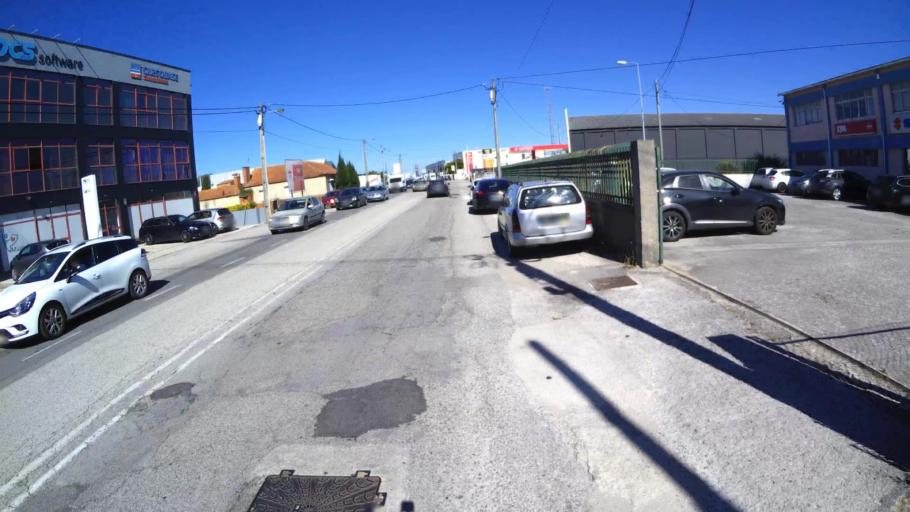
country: PT
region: Aveiro
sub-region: Aveiro
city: Aveiro
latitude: 40.6518
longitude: -8.6123
